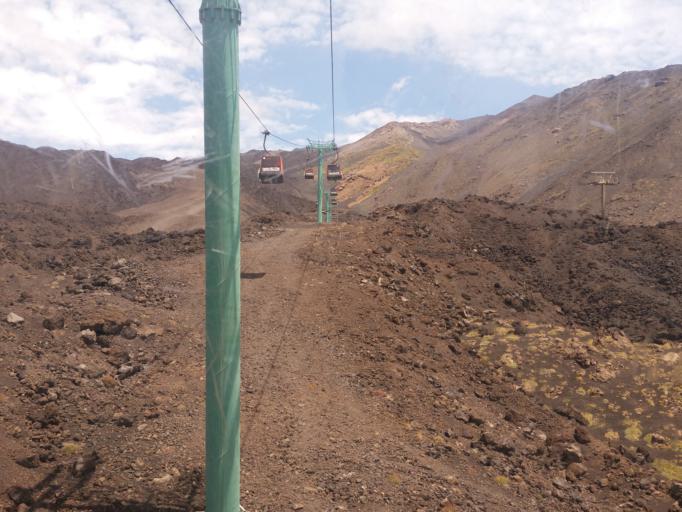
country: IT
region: Sicily
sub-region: Catania
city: Ragalna
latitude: 37.7055
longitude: 14.9993
